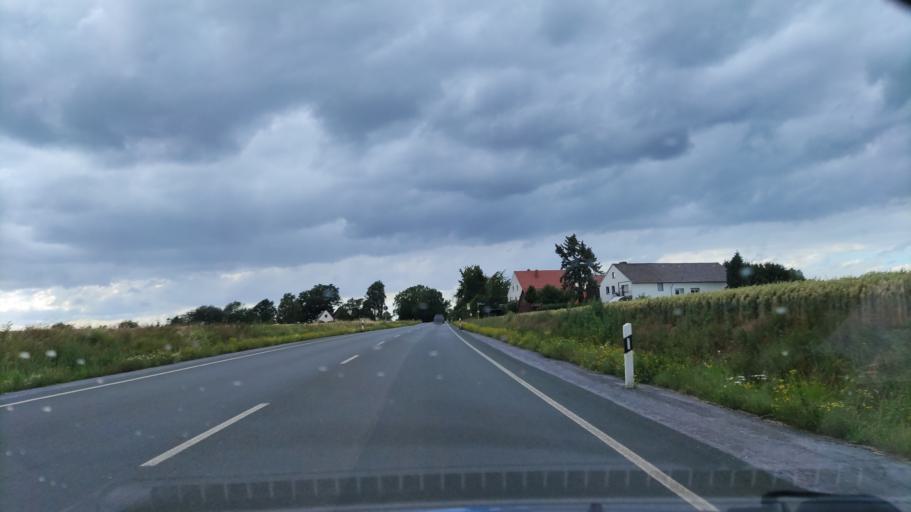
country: DE
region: North Rhine-Westphalia
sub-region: Regierungsbezirk Arnsberg
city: Soest
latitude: 51.5915
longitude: 8.0770
